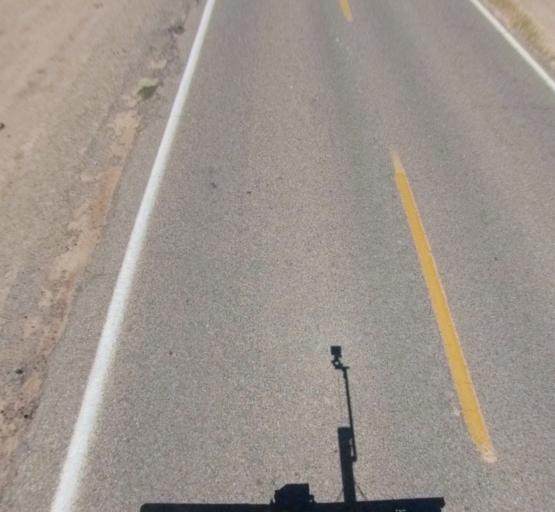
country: US
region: California
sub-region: Madera County
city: Fairmead
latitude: 37.0183
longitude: -120.2367
